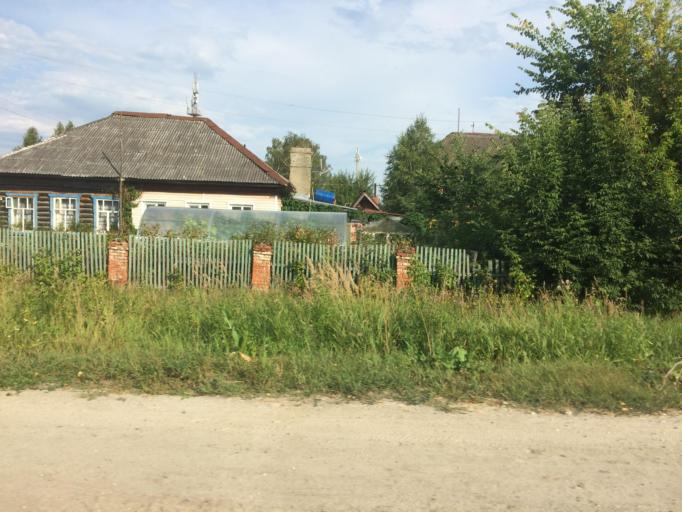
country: RU
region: Mariy-El
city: Yoshkar-Ola
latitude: 56.5502
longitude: 47.9840
